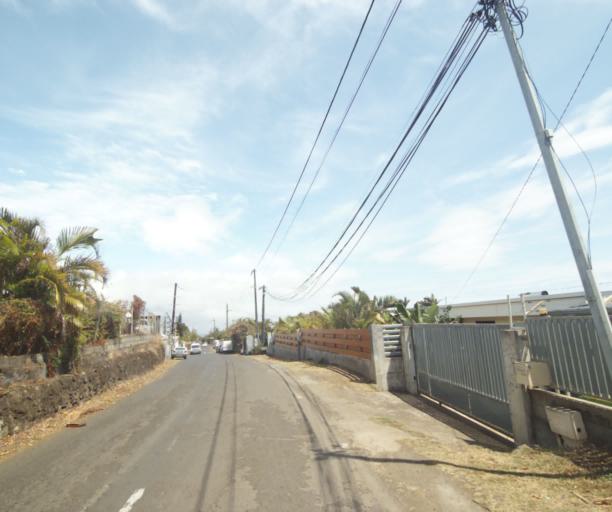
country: RE
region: Reunion
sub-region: Reunion
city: Trois-Bassins
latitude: -21.0850
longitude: 55.2718
